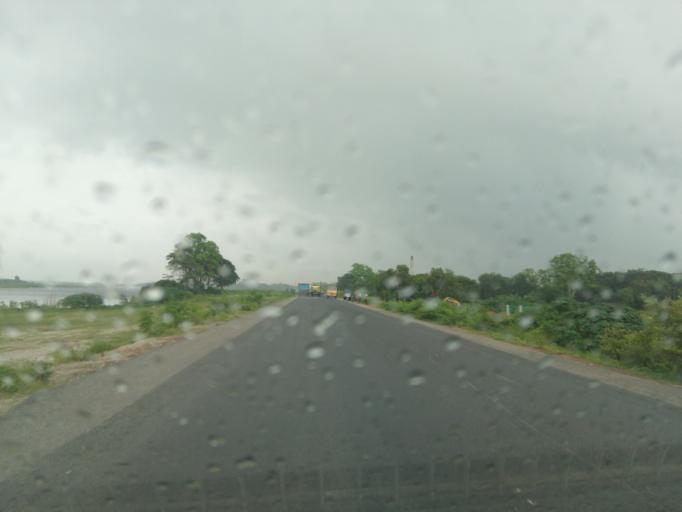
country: BD
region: Dhaka
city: Char Bhadrasan
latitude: 23.3696
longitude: 90.0758
